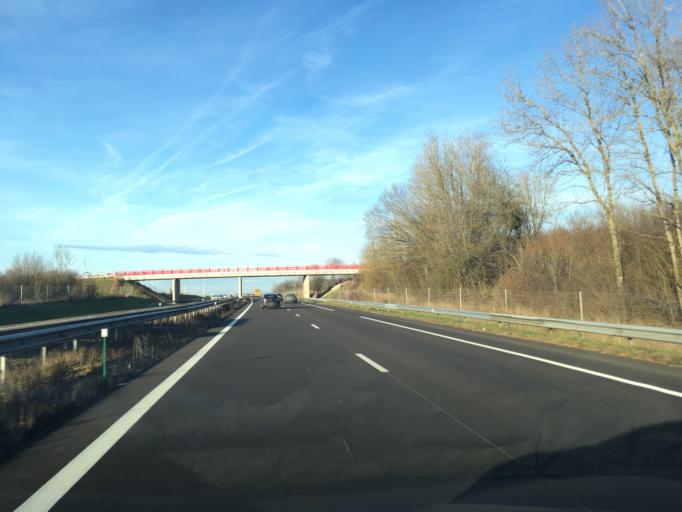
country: FR
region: Bourgogne
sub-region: Departement de l'Yonne
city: Joux-la-Ville
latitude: 47.6126
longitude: 3.9097
